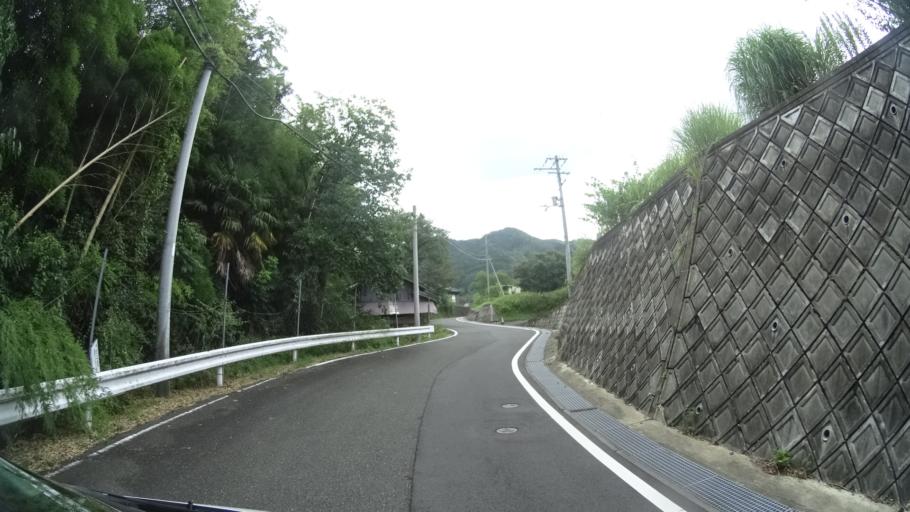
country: JP
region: Kyoto
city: Ayabe
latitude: 35.2720
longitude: 135.3483
